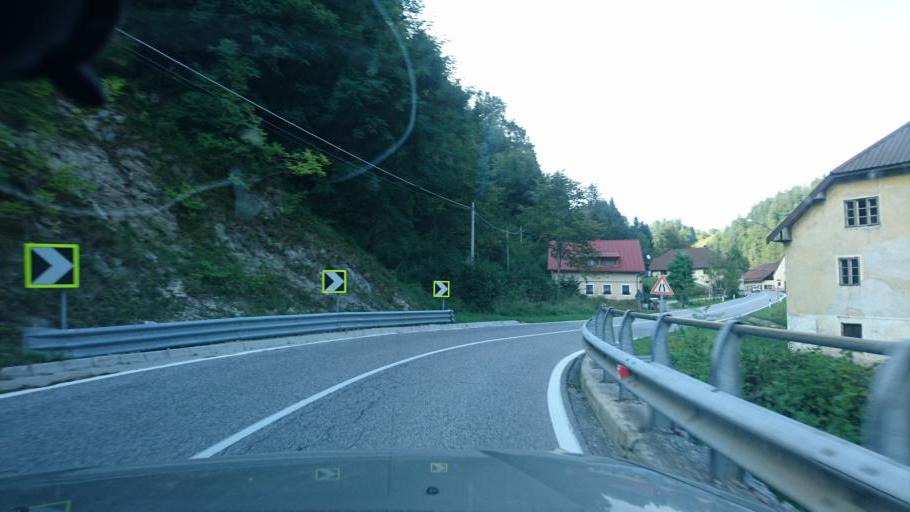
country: IT
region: Friuli Venezia Giulia
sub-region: Provincia di Udine
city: Tarvisio
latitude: 46.4884
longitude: 13.5840
